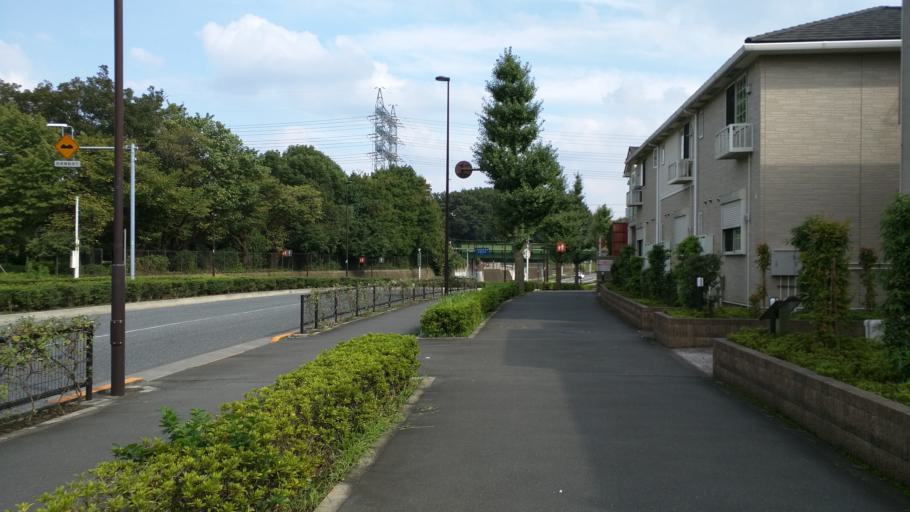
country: JP
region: Tokyo
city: Kamirenjaku
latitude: 35.6868
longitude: 139.5204
